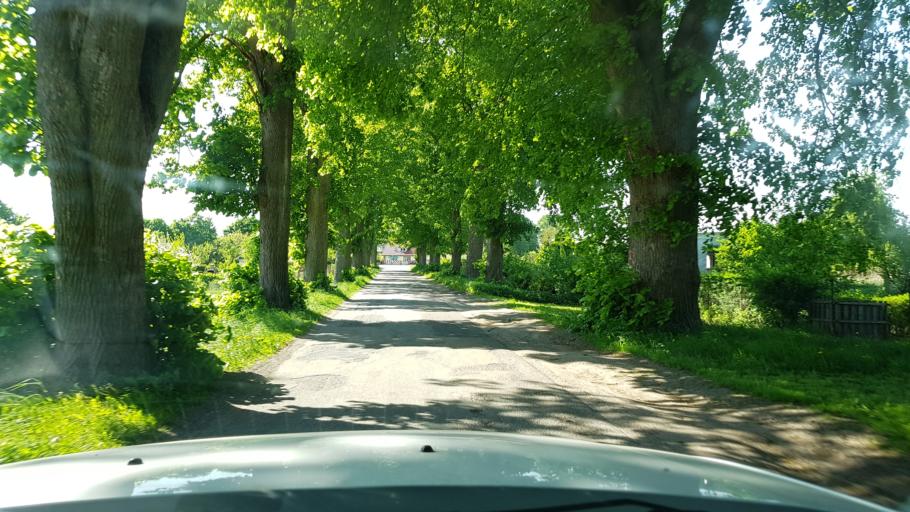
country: PL
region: West Pomeranian Voivodeship
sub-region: Powiat kolobrzeski
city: Ryman
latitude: 53.9993
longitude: 15.4968
